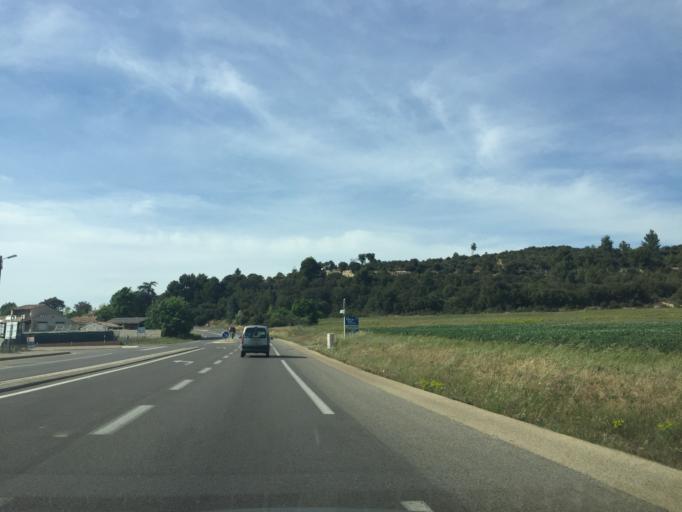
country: FR
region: Provence-Alpes-Cote d'Azur
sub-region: Departement du Var
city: Vinon-sur-Verdon
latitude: 43.7356
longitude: 5.8043
